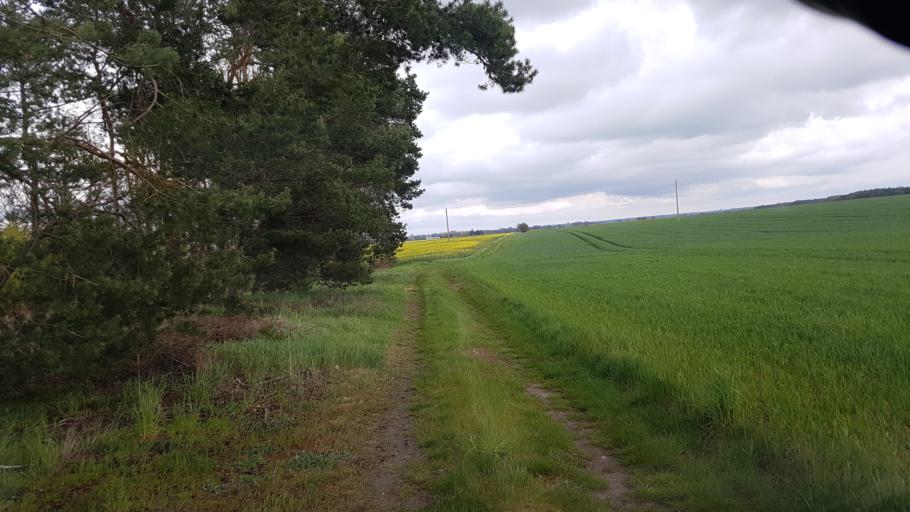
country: DE
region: Brandenburg
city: Schonborn
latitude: 51.6745
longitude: 13.4749
